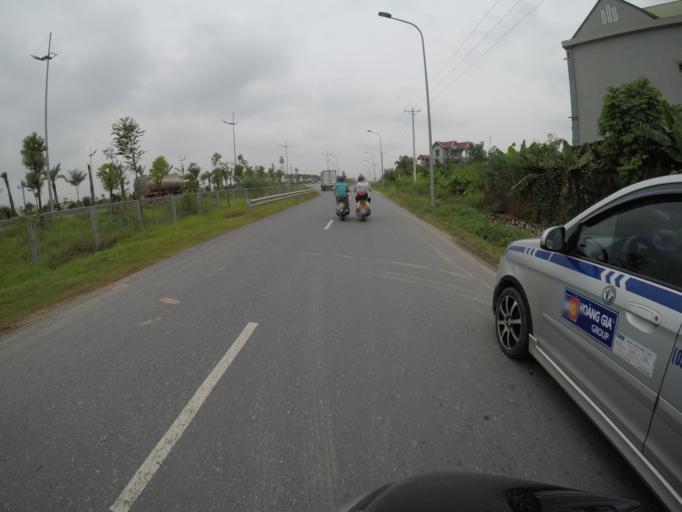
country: VN
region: Ha Noi
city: Dong Anh
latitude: 21.1780
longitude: 105.8265
